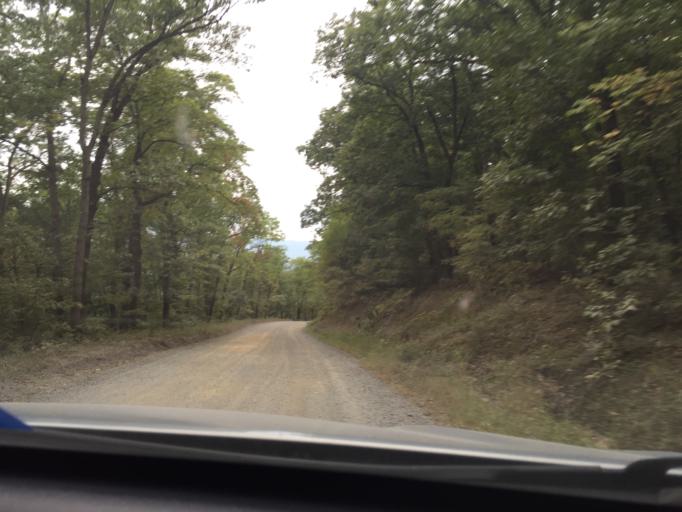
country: US
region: Virginia
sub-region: Shenandoah County
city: Woodstock
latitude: 38.8724
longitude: -78.4583
